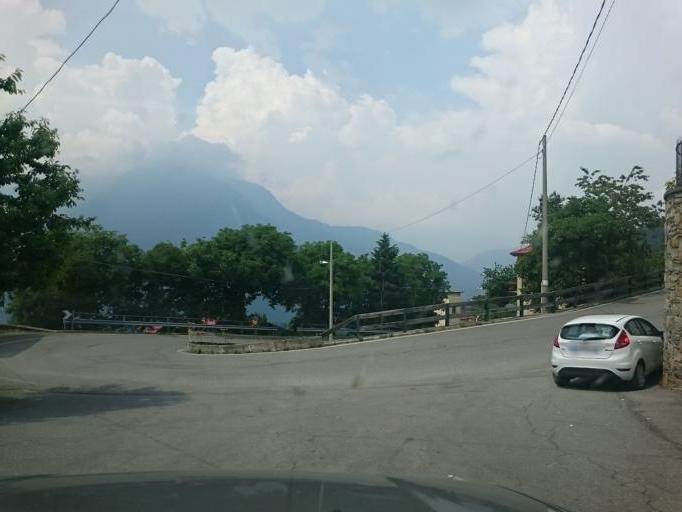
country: IT
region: Lombardy
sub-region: Provincia di Brescia
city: Cimbergo
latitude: 46.0230
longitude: 10.3669
